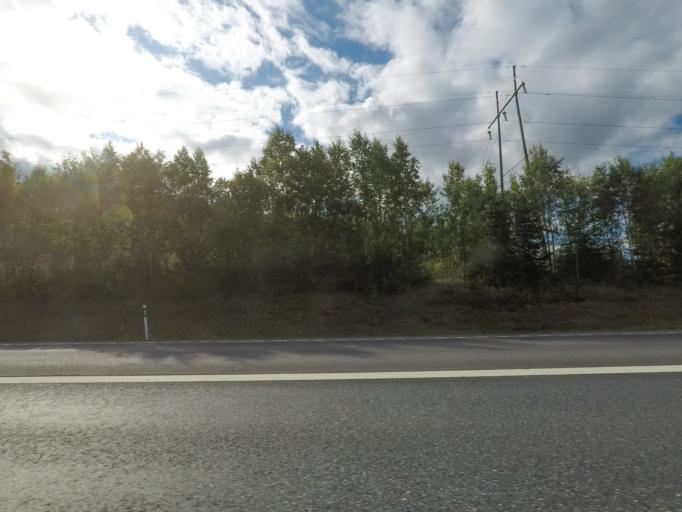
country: FI
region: Uusimaa
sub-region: Helsinki
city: Maentsaelae
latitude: 60.6078
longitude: 25.2601
